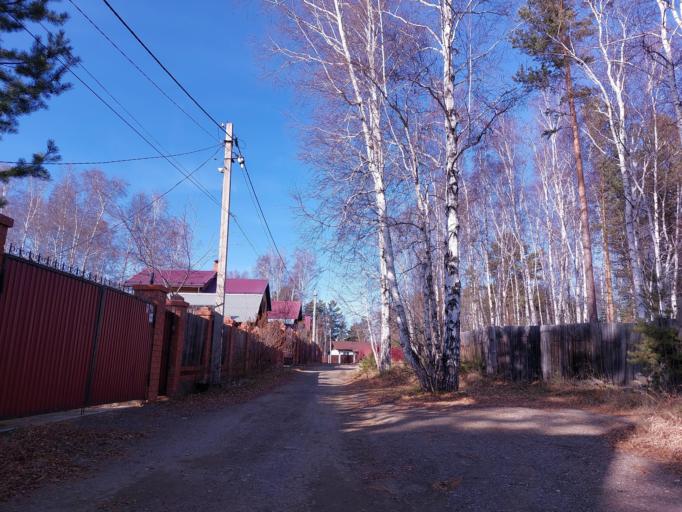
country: RU
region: Irkutsk
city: Pivovarikha
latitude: 52.1868
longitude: 104.4550
